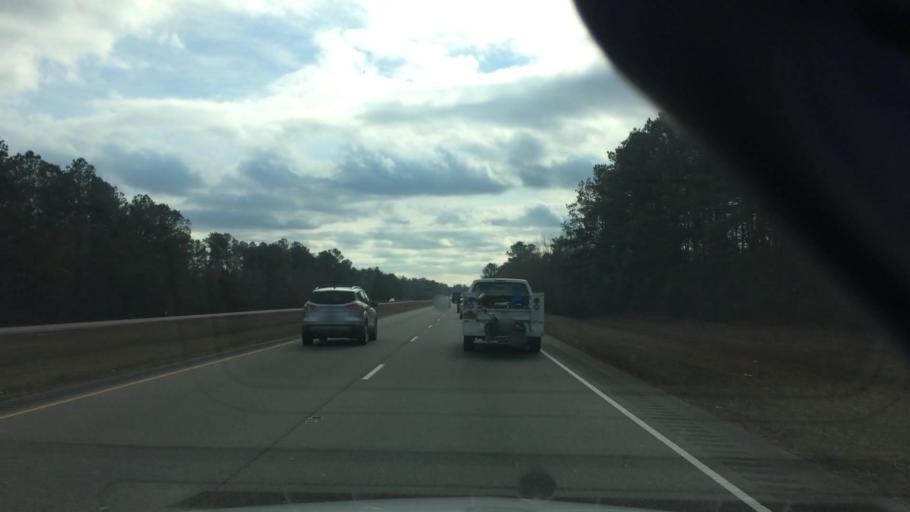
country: US
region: North Carolina
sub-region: Brunswick County
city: Leland
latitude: 34.1683
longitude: -78.0889
